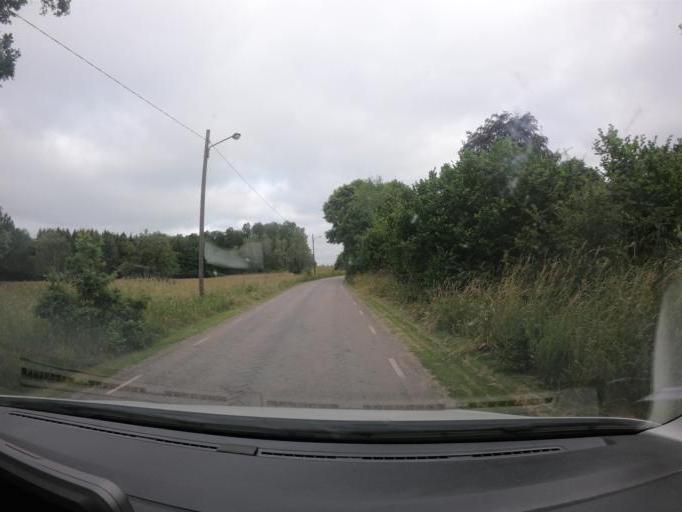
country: SE
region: Skane
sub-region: Klippans Kommun
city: Ljungbyhed
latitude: 56.0465
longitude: 13.2583
